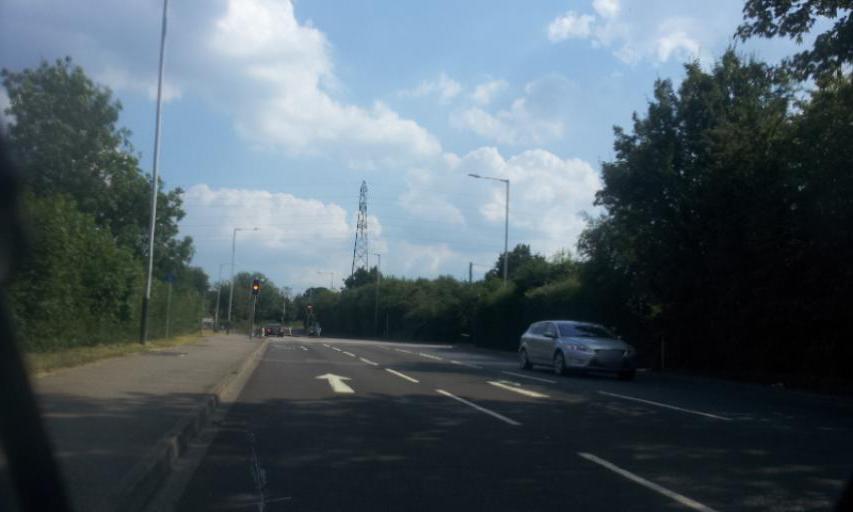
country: GB
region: England
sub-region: Kent
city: Paddock Wood
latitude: 51.1724
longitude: 0.3851
